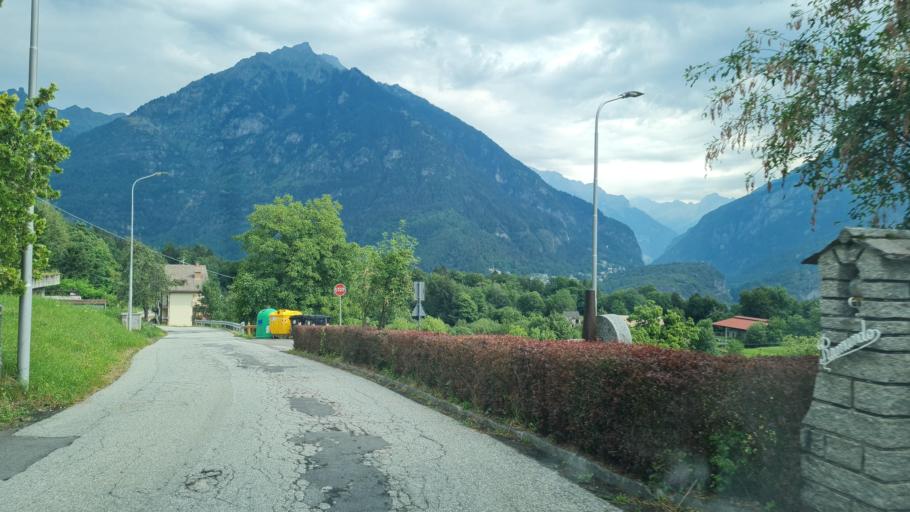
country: IT
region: Piedmont
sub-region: Provincia Verbano-Cusio-Ossola
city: Baceno
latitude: 46.2425
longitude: 8.3145
